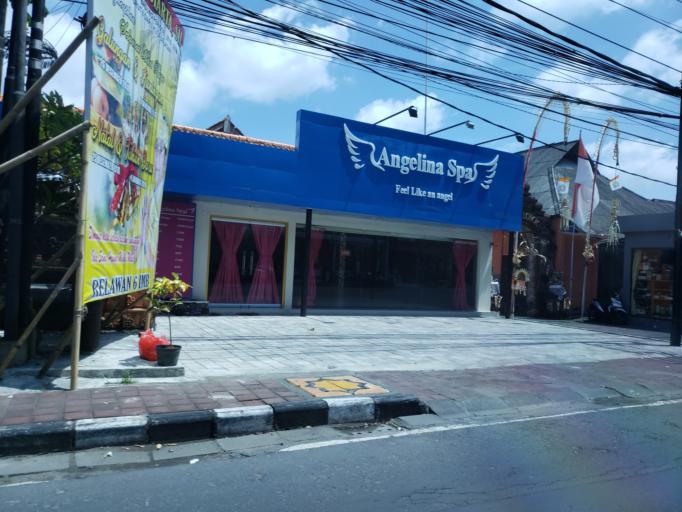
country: ID
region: Bali
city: Jimbaran
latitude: -8.7787
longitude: 115.1687
